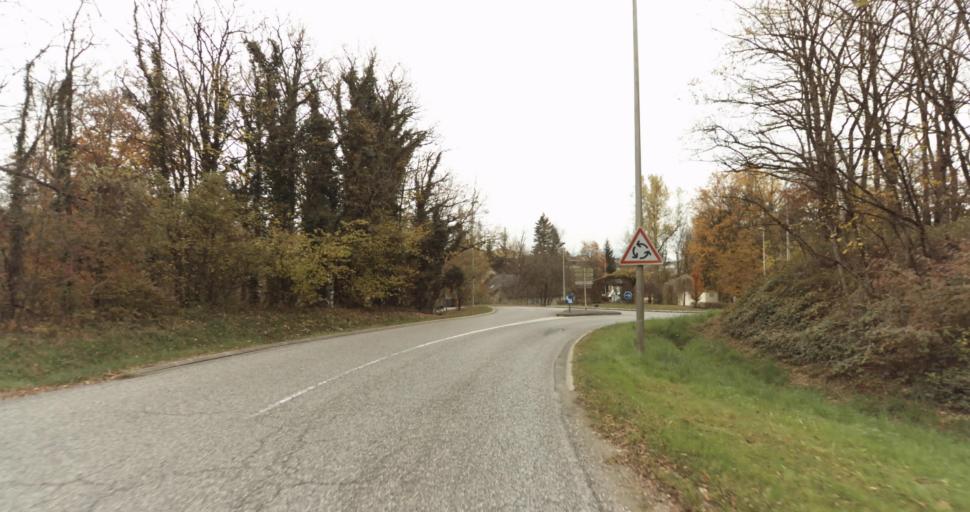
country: FR
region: Rhone-Alpes
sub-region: Departement de la Haute-Savoie
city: Pringy
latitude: 45.9528
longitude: 6.1160
